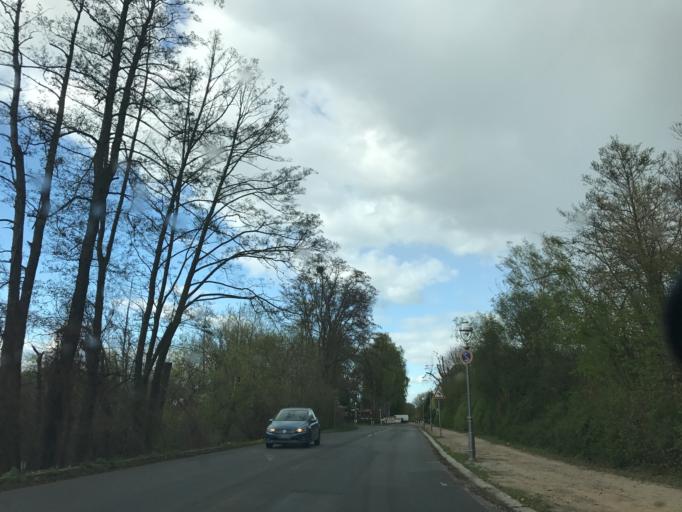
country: DE
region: Berlin
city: Haselhorst
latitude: 52.5493
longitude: 13.2360
